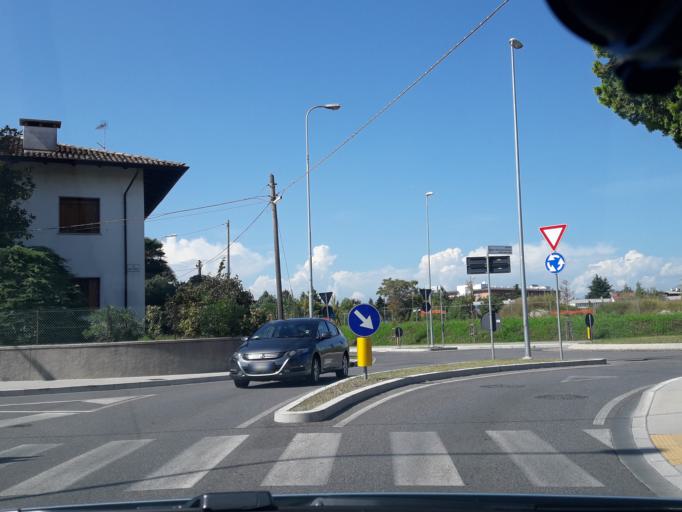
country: IT
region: Friuli Venezia Giulia
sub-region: Provincia di Udine
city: Udine
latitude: 46.0648
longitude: 13.2196
